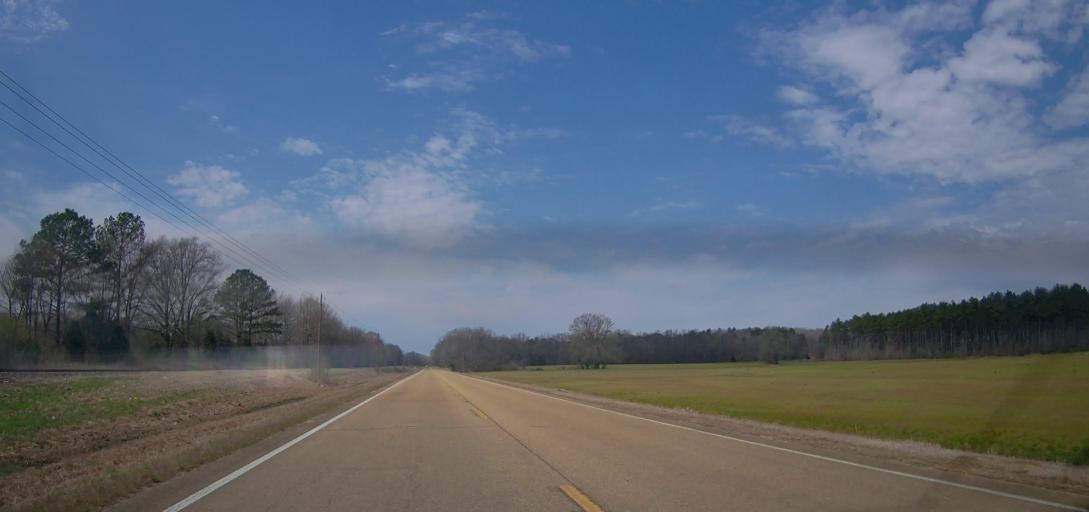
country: US
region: Mississippi
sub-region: Benton County
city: Ashland
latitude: 34.6244
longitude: -89.2483
